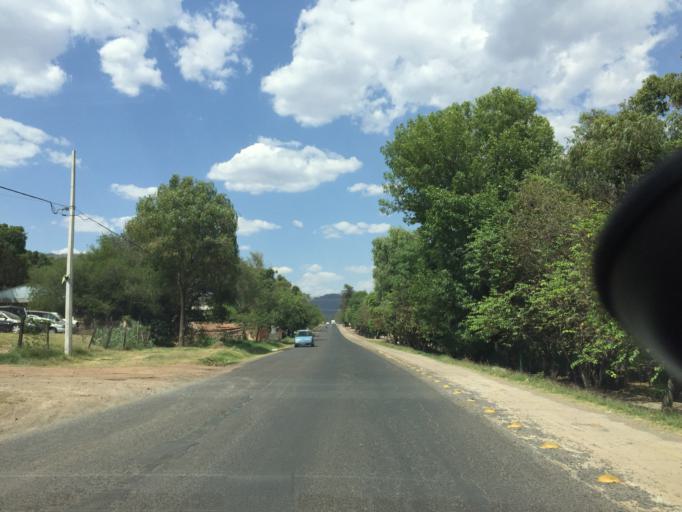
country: MX
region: Jalisco
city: Atotonilco el Alto
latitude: 20.5581
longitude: -102.4899
